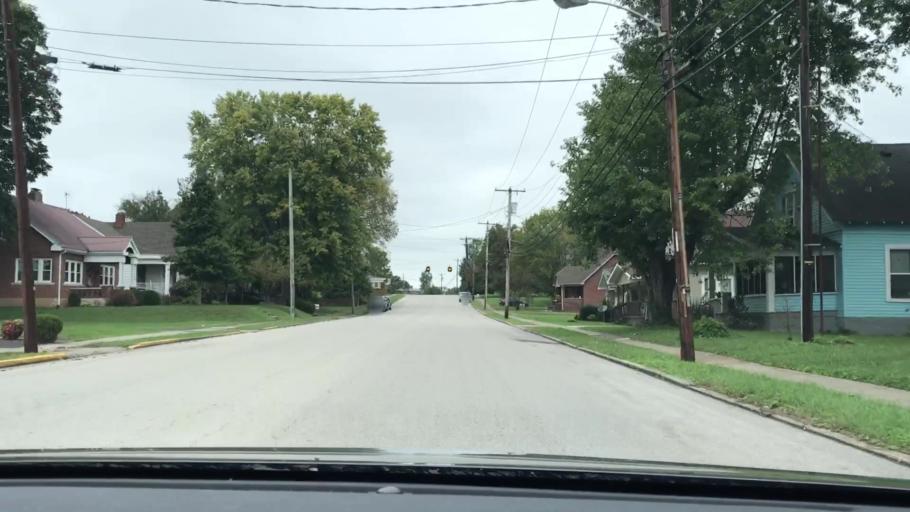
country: US
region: Kentucky
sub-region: Pulaski County
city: Somerset
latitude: 37.0869
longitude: -84.5991
